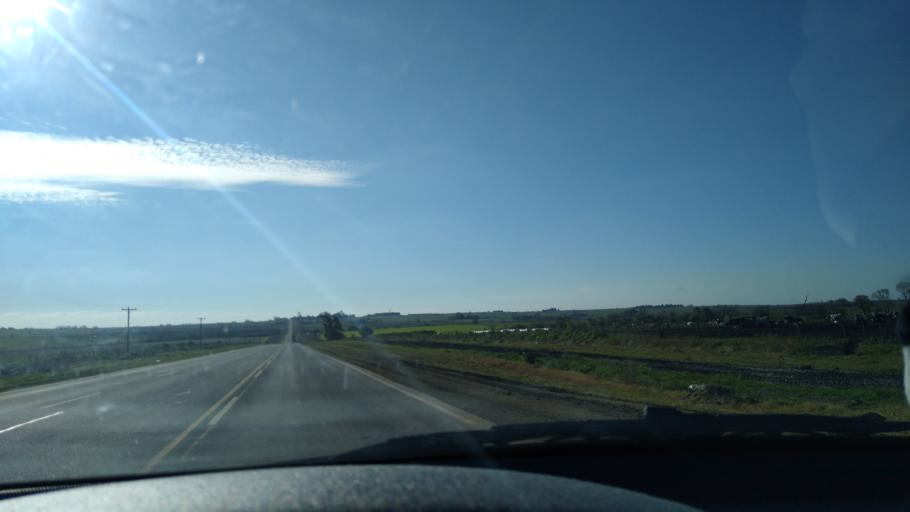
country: AR
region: Entre Rios
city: Aranguren
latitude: -32.3865
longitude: -60.3338
